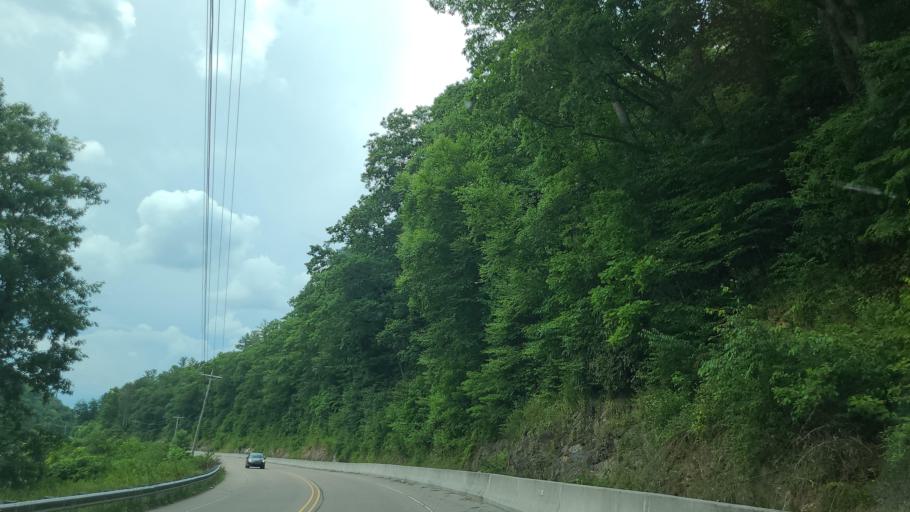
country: US
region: North Carolina
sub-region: Ashe County
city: Jefferson
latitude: 36.3754
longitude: -81.3978
